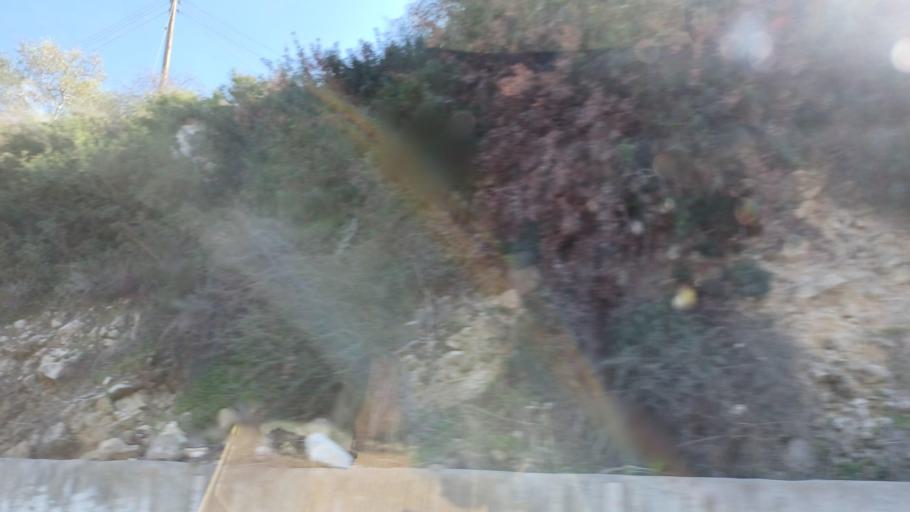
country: CY
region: Larnaka
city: Agios Tychon
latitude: 34.7297
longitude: 33.1441
